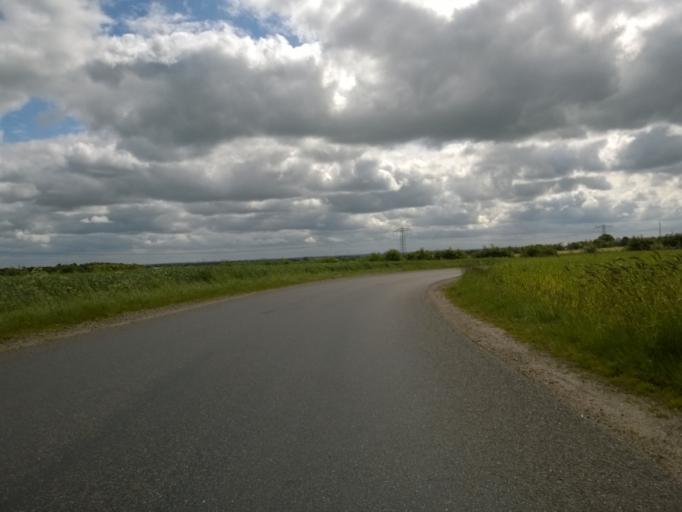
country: DK
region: Central Jutland
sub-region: Holstebro Kommune
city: Vinderup
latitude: 56.4070
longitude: 8.8145
